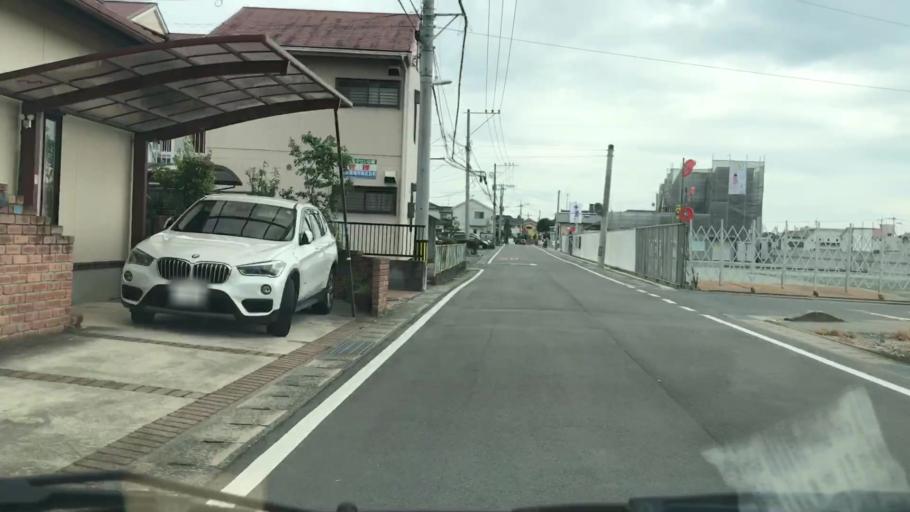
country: JP
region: Saga Prefecture
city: Saga-shi
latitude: 33.2755
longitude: 130.2636
